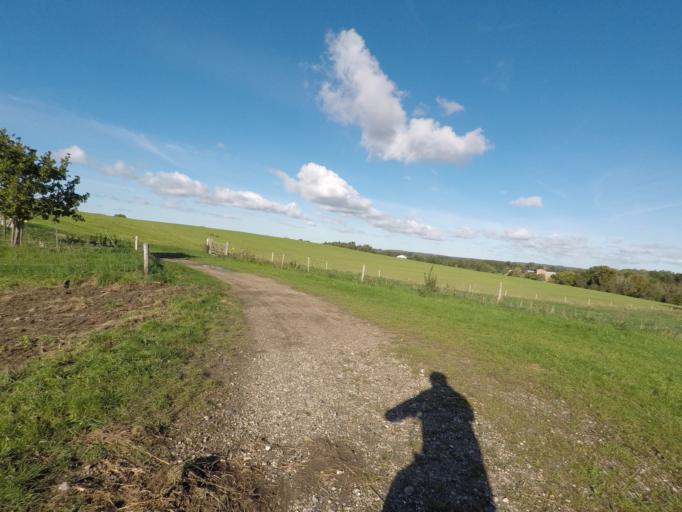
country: DK
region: Capital Region
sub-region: Ballerup Kommune
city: Malov
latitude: 55.7579
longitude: 12.3137
